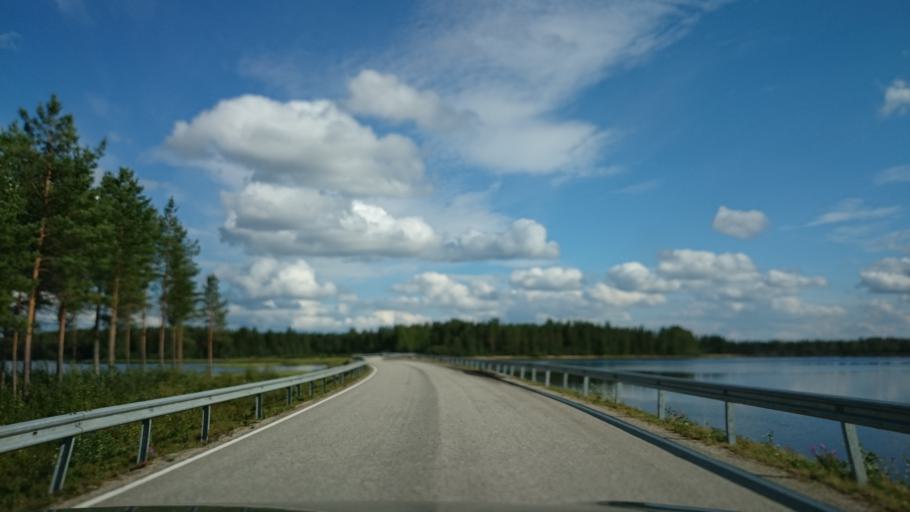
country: FI
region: Kainuu
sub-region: Kehys-Kainuu
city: Suomussalmi
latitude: 64.7616
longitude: 29.3771
